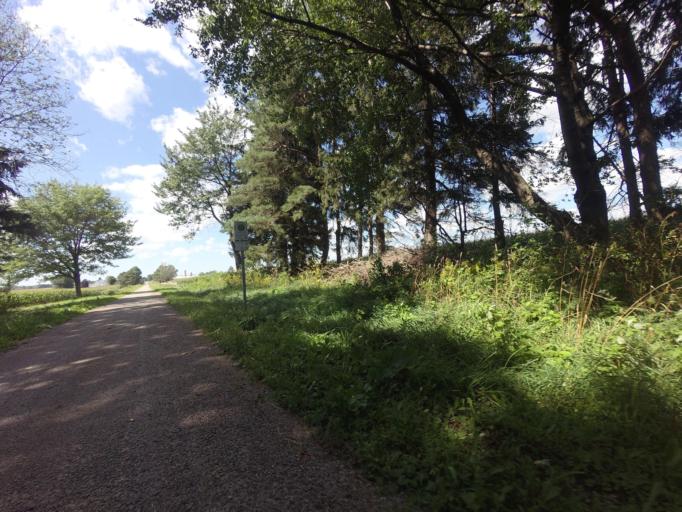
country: CA
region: Ontario
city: Huron East
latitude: 43.6612
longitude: -81.2533
